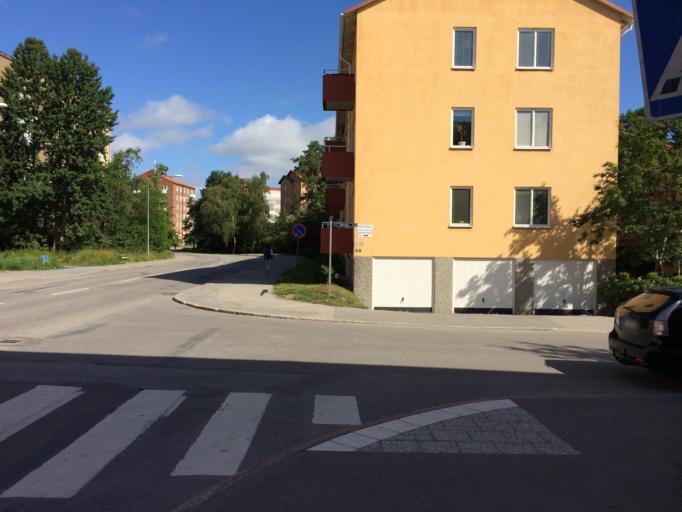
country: SE
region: Stockholm
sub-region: Huddinge Kommun
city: Segeltorp
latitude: 59.2983
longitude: 17.9828
